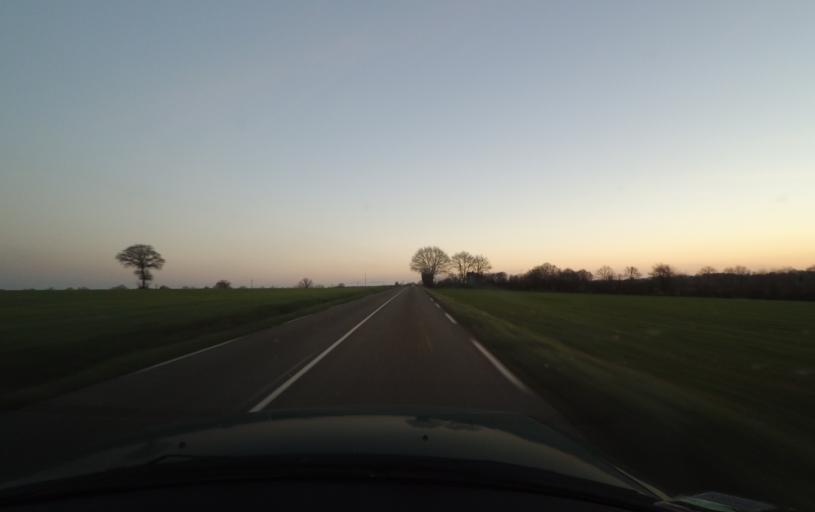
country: FR
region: Pays de la Loire
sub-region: Departement de la Mayenne
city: Soulge-sur-Ouette
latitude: 48.0903
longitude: -0.5305
